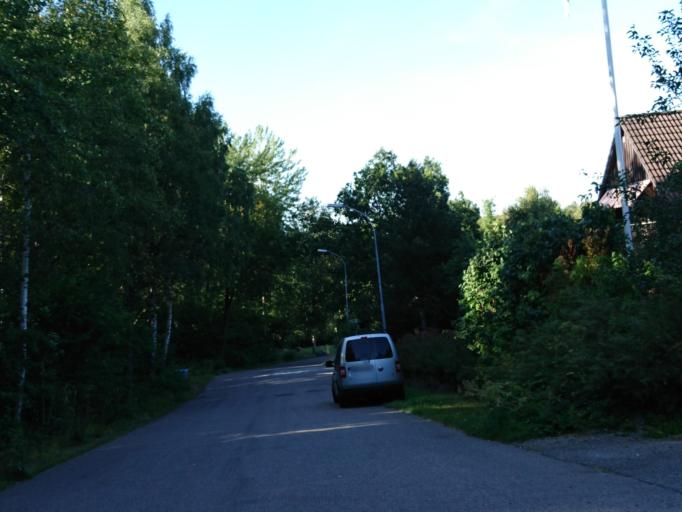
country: SE
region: Stockholm
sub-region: Huddinge Kommun
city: Segeltorp
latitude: 59.2718
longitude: 17.9454
